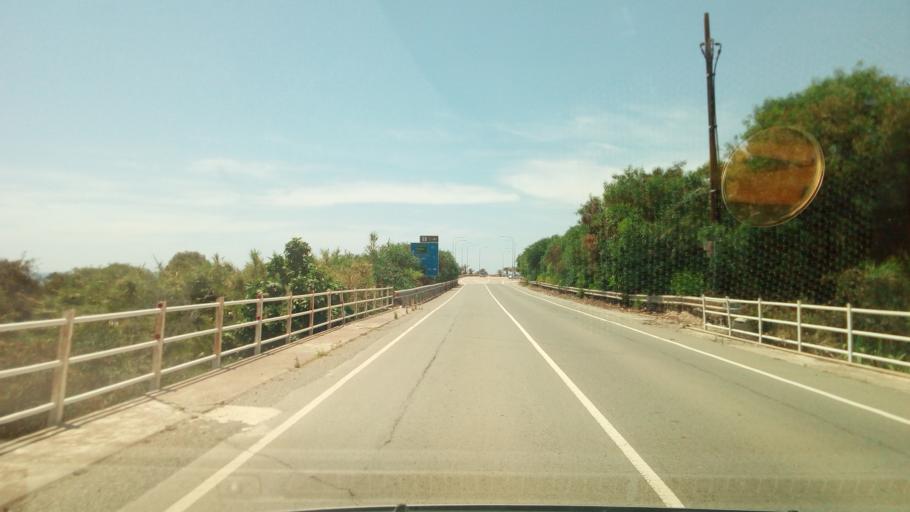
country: CY
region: Limassol
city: Pissouri
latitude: 34.6837
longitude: 32.5898
